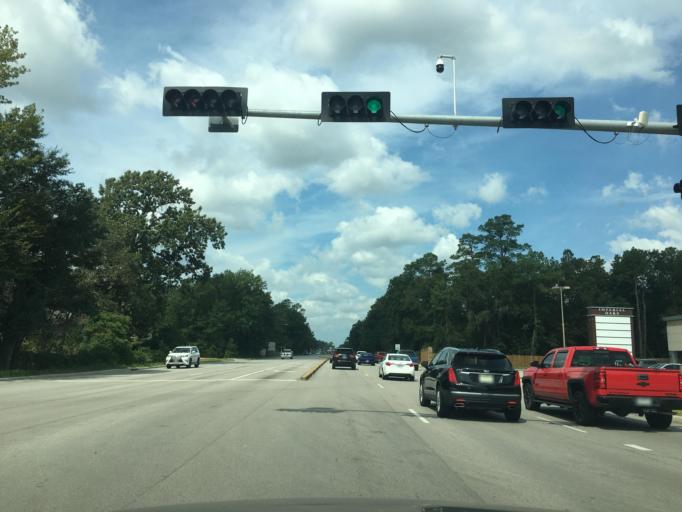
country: US
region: Texas
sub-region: Harris County
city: Spring
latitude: 30.1235
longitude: -95.4105
